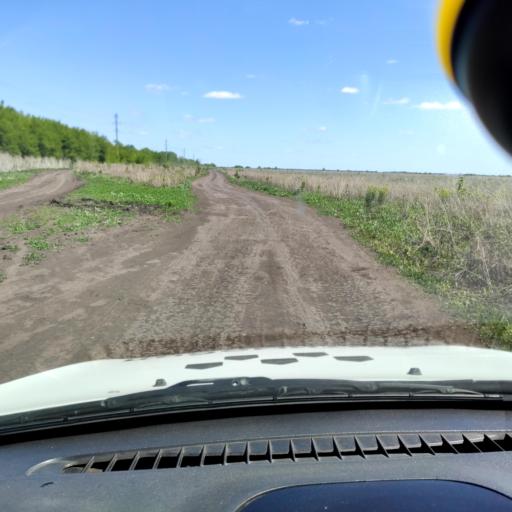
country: RU
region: Samara
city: Tol'yatti
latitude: 53.5968
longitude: 49.4683
